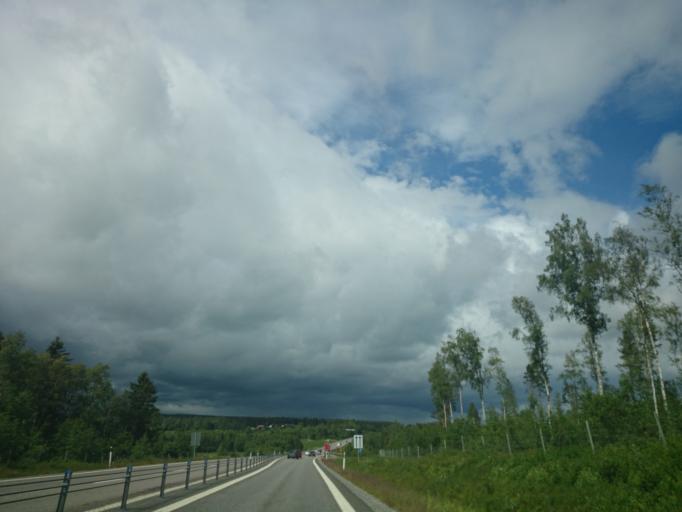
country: SE
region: Vaesternorrland
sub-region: Sundsvalls Kommun
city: Njurundabommen
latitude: 62.2201
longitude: 17.3722
